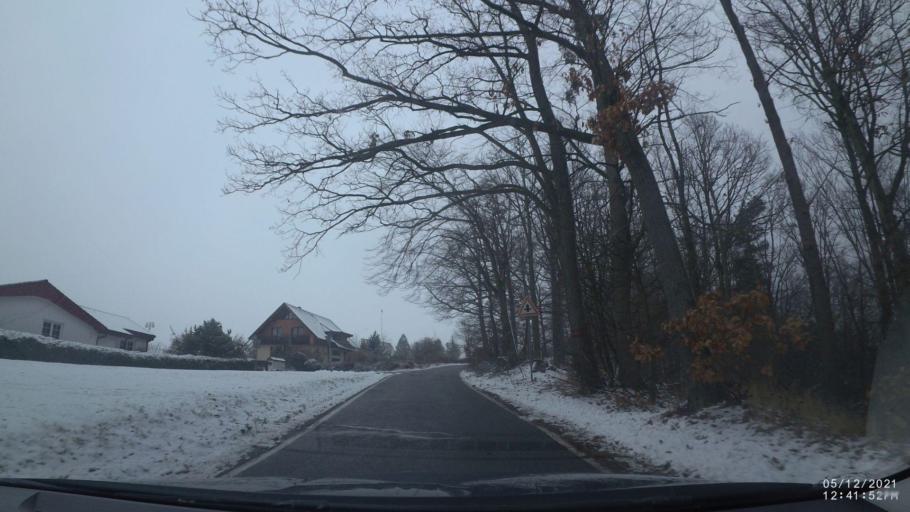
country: CZ
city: Nove Mesto nad Metuji
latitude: 50.3583
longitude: 16.1604
